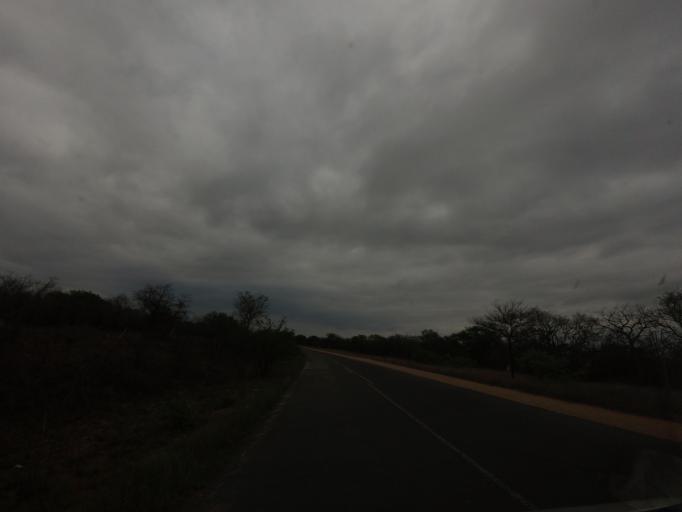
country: ZA
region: Mpumalanga
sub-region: Ehlanzeni District
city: Komatipoort
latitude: -25.4842
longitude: 31.6753
